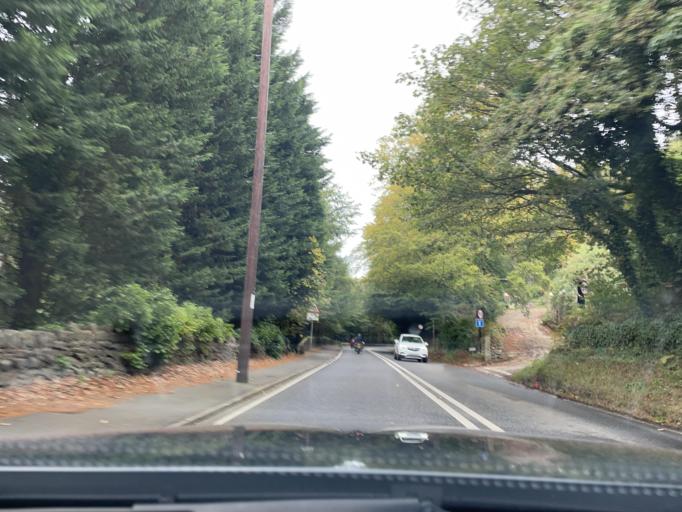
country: GB
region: England
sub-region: Sheffield
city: Bradfield
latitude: 53.3806
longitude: -1.5957
